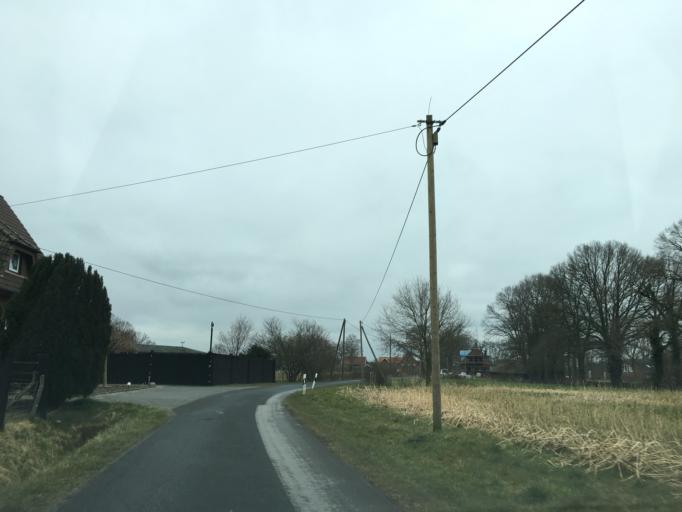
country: DE
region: North Rhine-Westphalia
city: Ludinghausen
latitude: 51.7654
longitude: 7.4713
